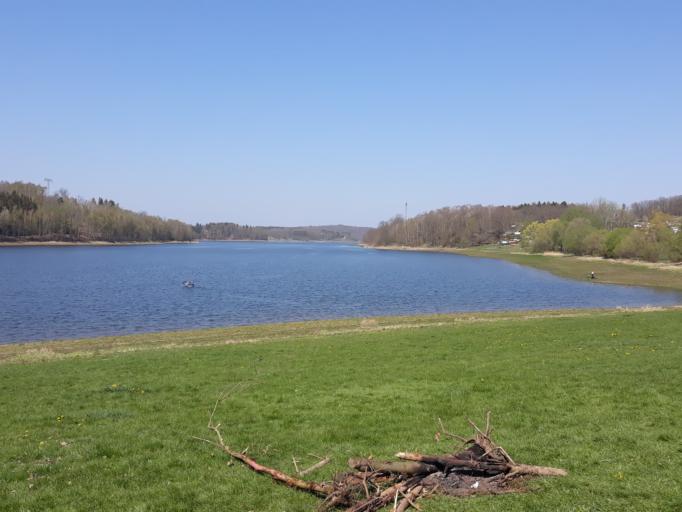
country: DE
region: Saxony
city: Neuensalz
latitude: 50.5250
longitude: 12.2115
